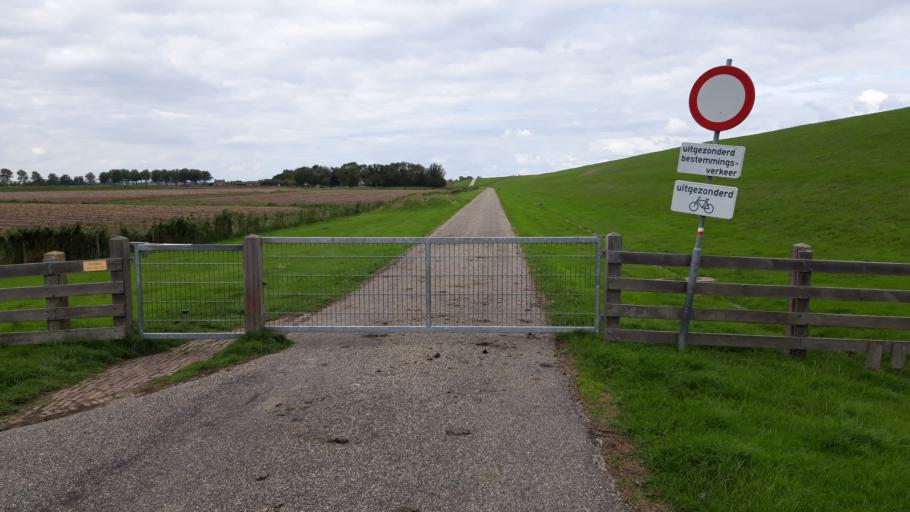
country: NL
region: Friesland
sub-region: Gemeente Dongeradeel
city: Anjum
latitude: 53.4004
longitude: 6.0978
